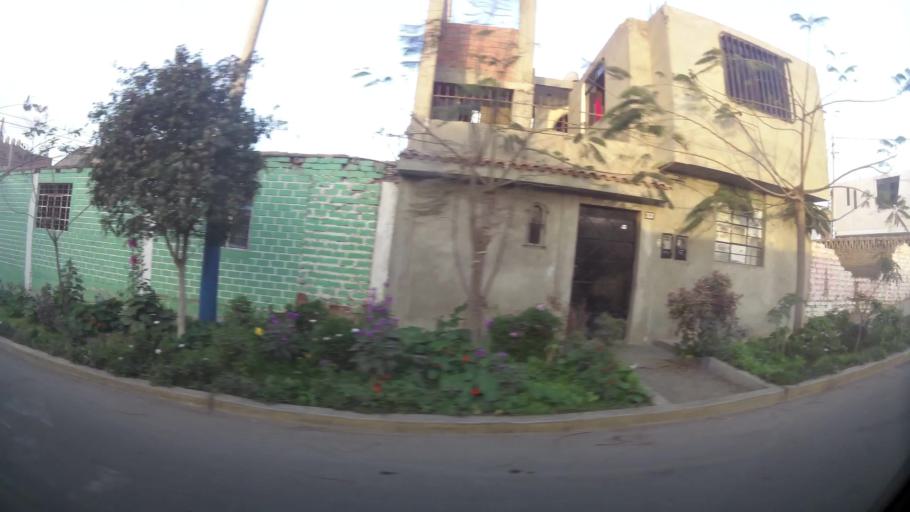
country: PE
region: Lima
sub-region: Huaura
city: Huacho
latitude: -11.1097
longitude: -77.6004
